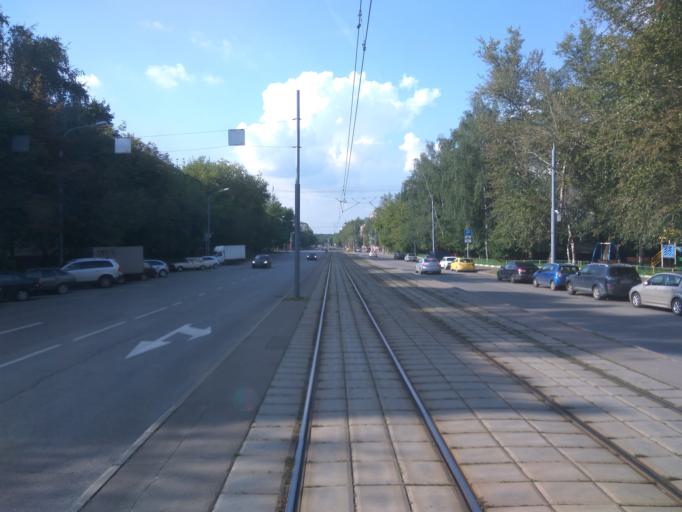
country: RU
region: Moscow
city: Perovo
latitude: 55.7568
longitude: 37.7890
